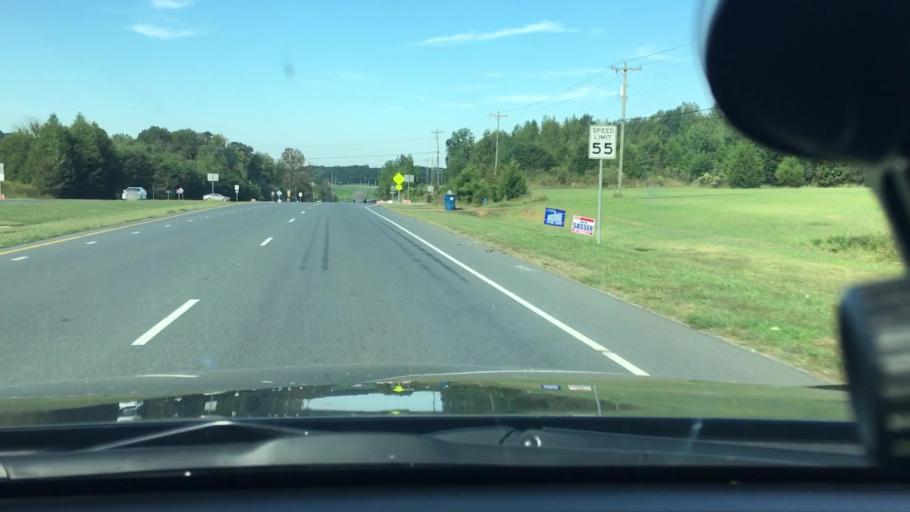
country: US
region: North Carolina
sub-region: Stanly County
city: Locust
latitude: 35.2540
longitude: -80.4670
